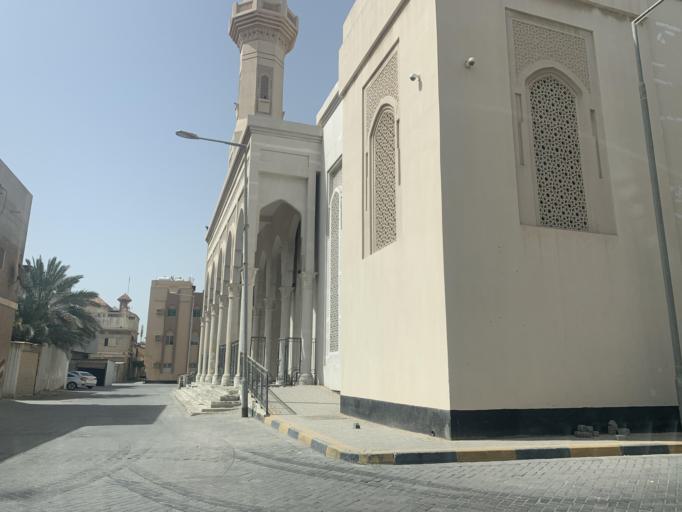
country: BH
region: Northern
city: Sitrah
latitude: 26.1613
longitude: 50.6084
